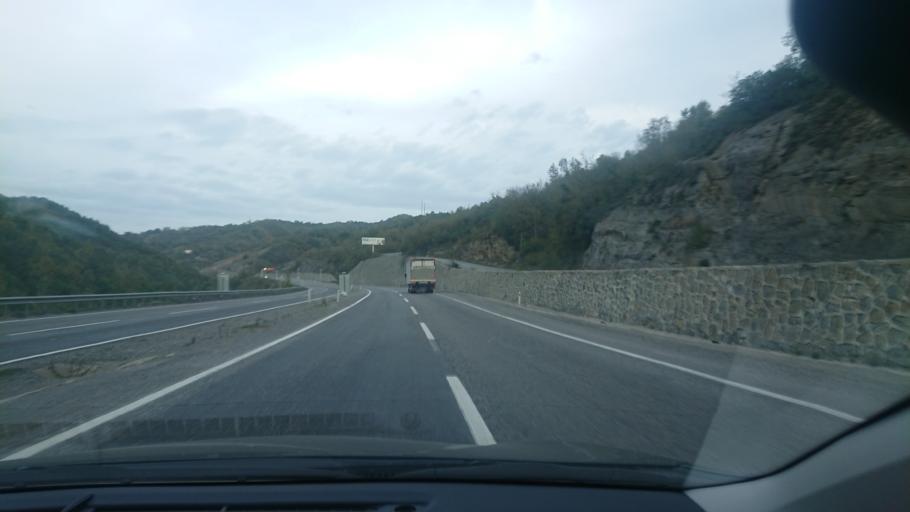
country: TR
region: Zonguldak
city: Beycuma
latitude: 41.4067
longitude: 31.9354
